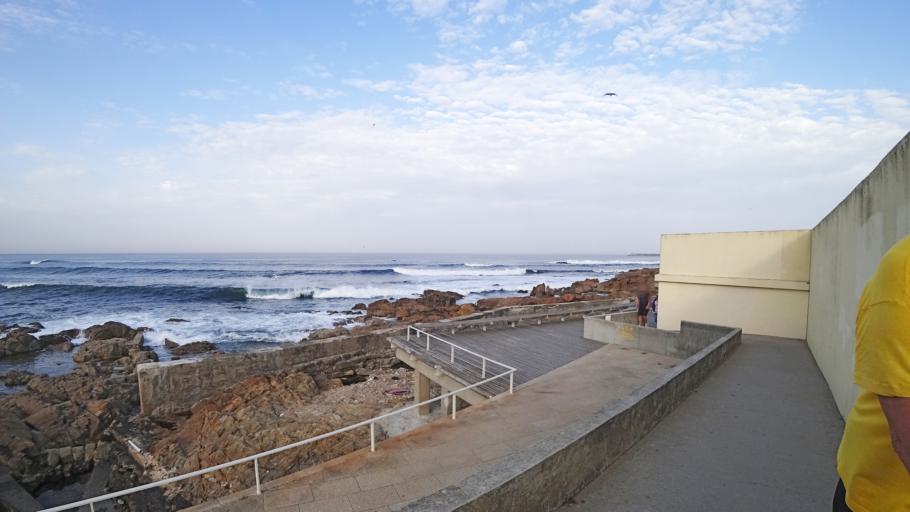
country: PT
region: Porto
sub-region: Matosinhos
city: Matosinhos
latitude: 41.1634
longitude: -8.6866
